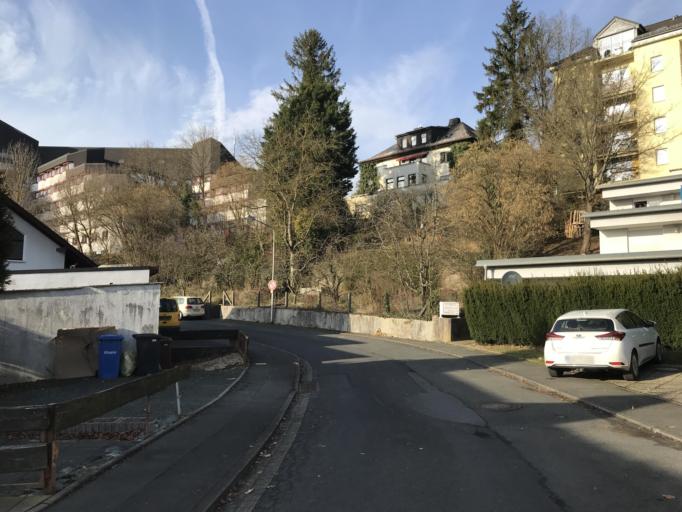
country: DE
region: Hesse
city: Weilburg
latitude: 50.4805
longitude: 8.2724
